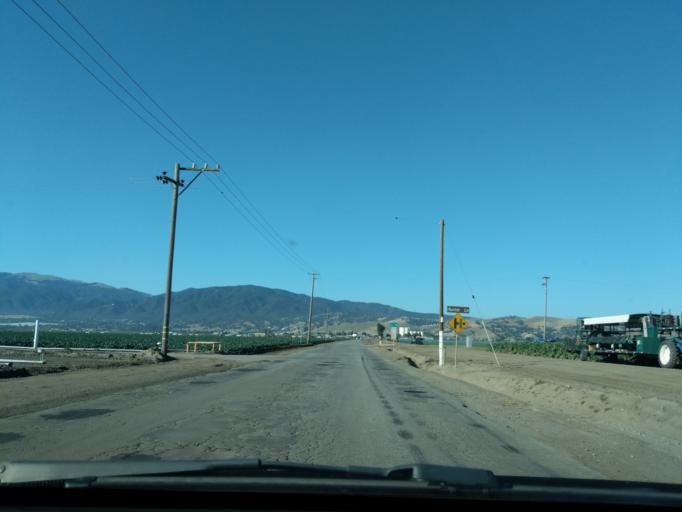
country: US
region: California
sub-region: Monterey County
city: Salinas
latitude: 36.6393
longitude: -121.6373
